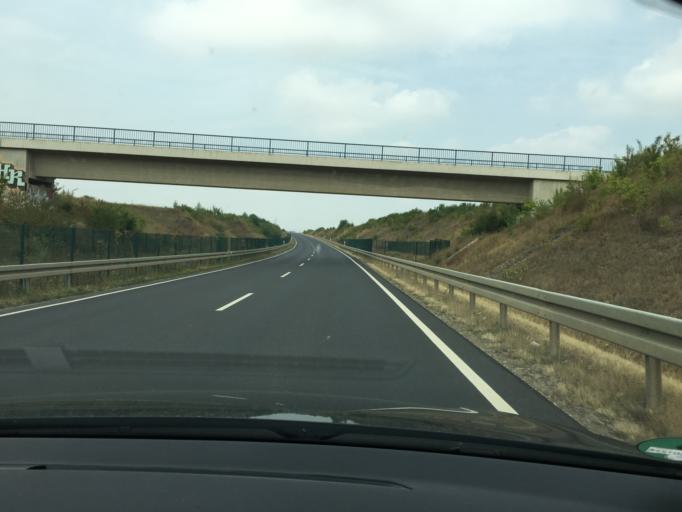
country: DE
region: North Rhine-Westphalia
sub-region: Regierungsbezirk Koln
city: Bergheim
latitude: 50.9012
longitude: 6.6301
